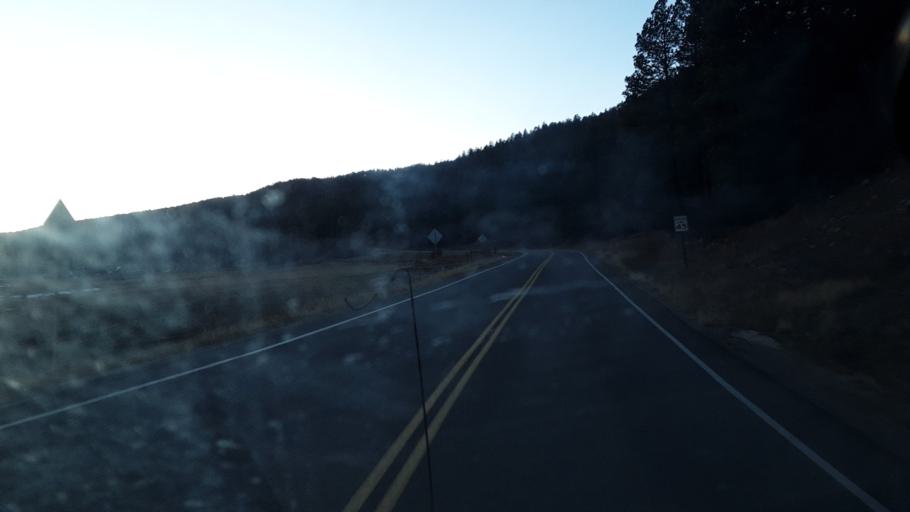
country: US
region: Colorado
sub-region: La Plata County
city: Bayfield
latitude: 37.3464
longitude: -107.7059
